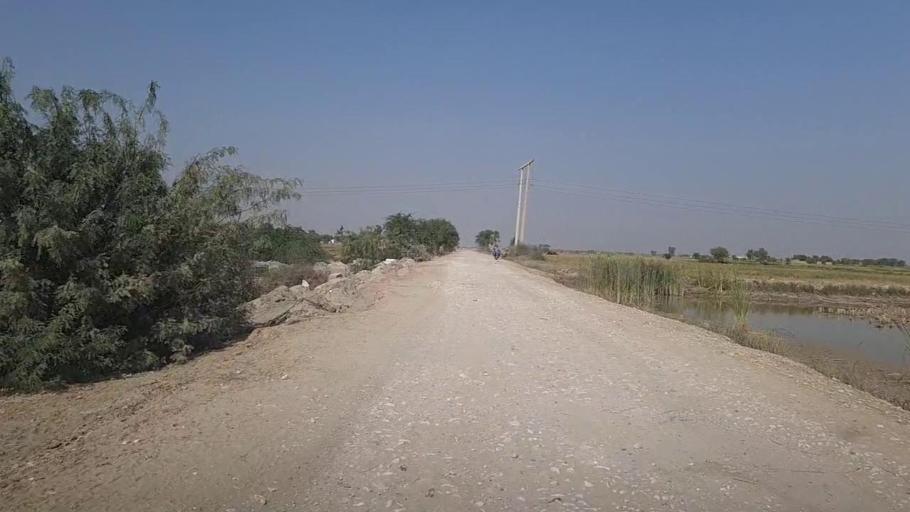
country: PK
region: Sindh
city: Kandhkot
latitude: 28.3912
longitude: 69.3267
